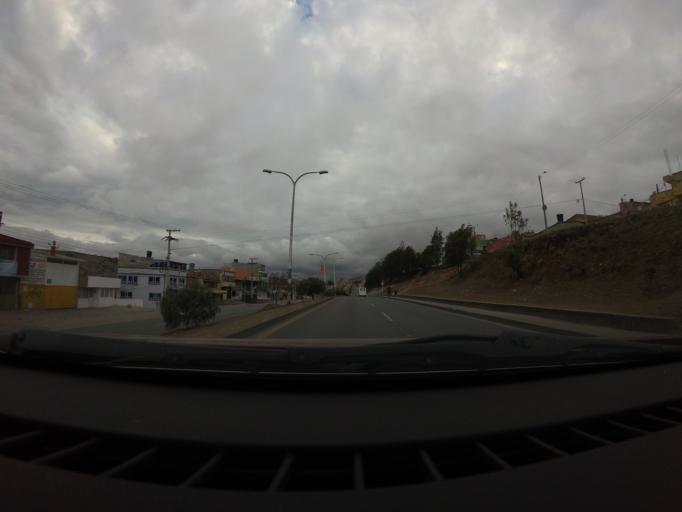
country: CO
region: Boyaca
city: Tunja
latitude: 5.5218
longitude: -73.3639
